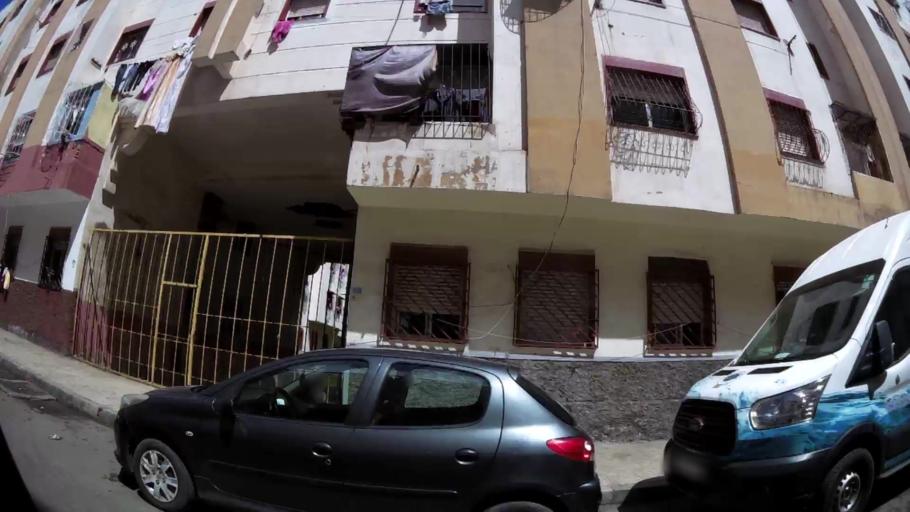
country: MA
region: Grand Casablanca
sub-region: Mediouna
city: Tit Mellil
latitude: 33.6010
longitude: -7.4794
